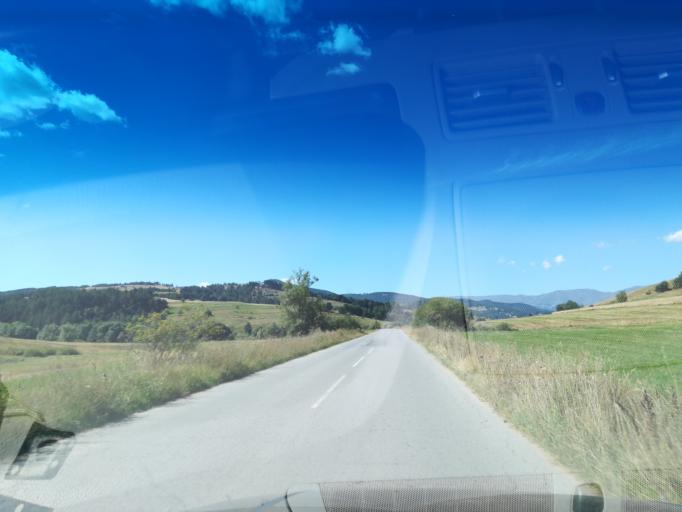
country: BG
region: Sofiya
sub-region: Obshtina Koprivshtitsa
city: Koprivshtitsa
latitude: 42.6049
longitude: 24.3794
